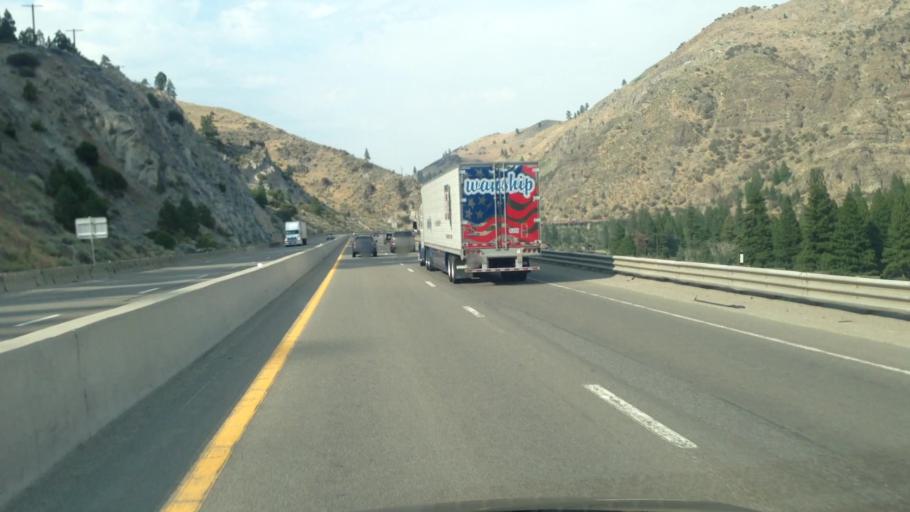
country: US
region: Nevada
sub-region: Washoe County
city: Verdi
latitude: 39.4691
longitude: -120.0020
